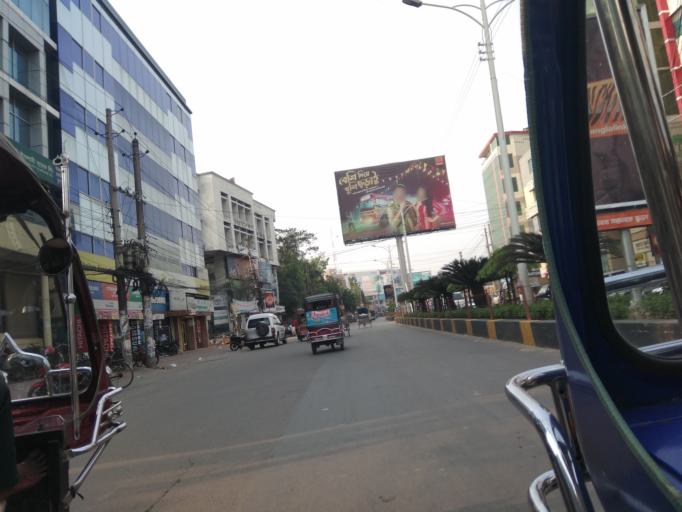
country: BD
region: Khulna
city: Khulna
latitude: 22.8203
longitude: 89.5529
